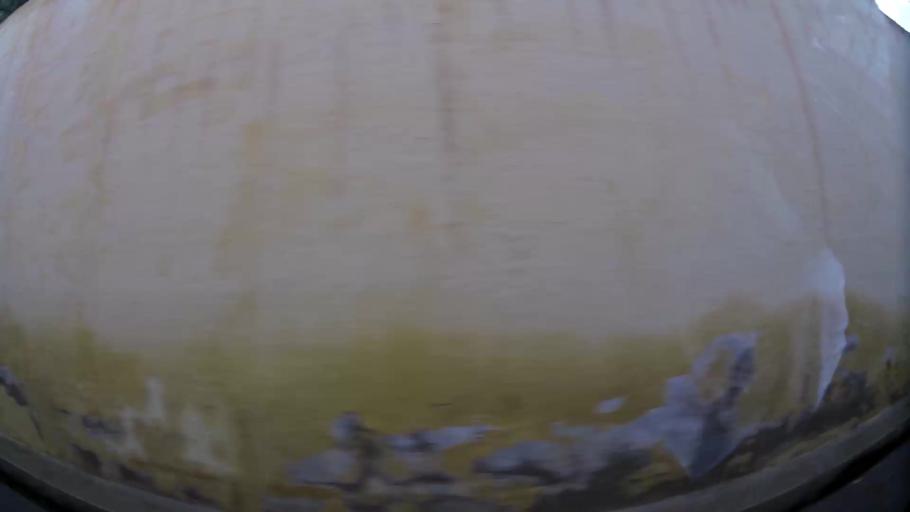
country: MA
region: Oriental
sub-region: Nador
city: Nador
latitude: 35.1467
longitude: -3.0033
